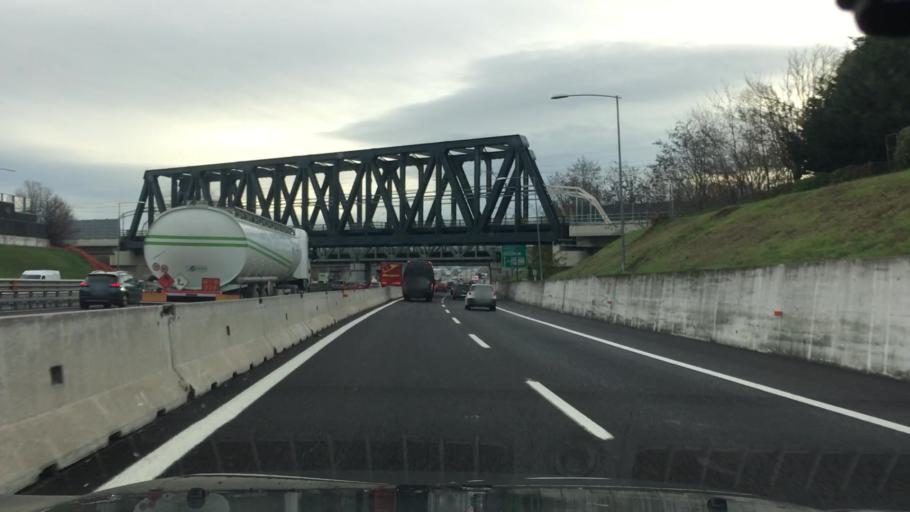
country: IT
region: Emilia-Romagna
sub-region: Provincia di Bologna
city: Trebbo
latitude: 44.5320
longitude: 11.3329
